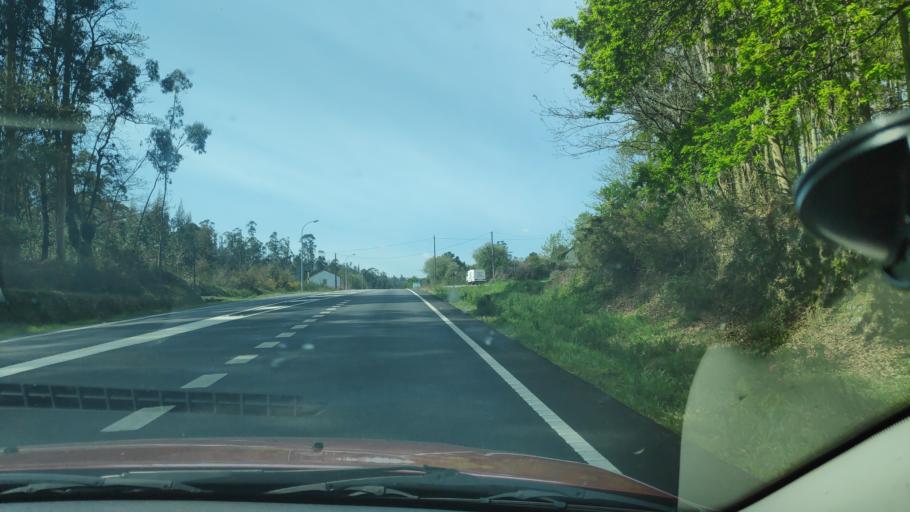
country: ES
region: Galicia
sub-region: Provincia da Coruna
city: Ames
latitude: 42.8791
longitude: -8.6769
